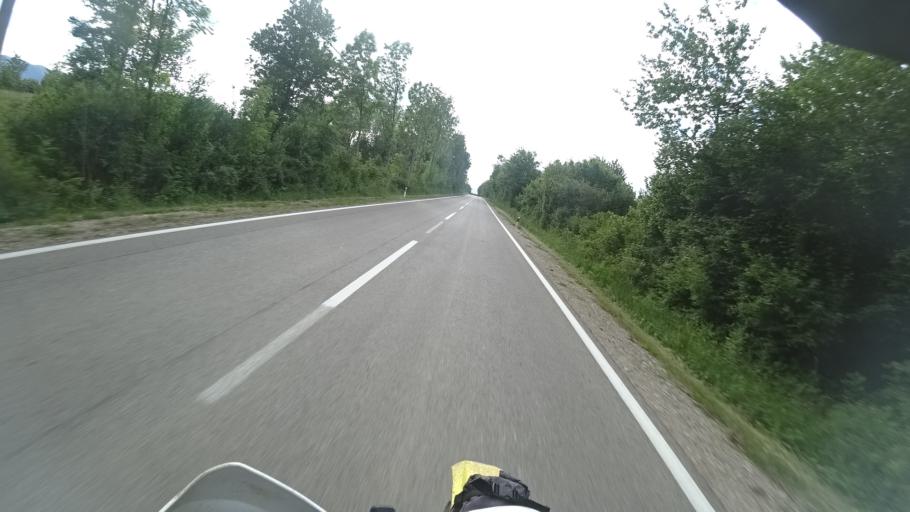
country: HR
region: Licko-Senjska
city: Gospic
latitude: 44.5079
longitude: 15.4397
